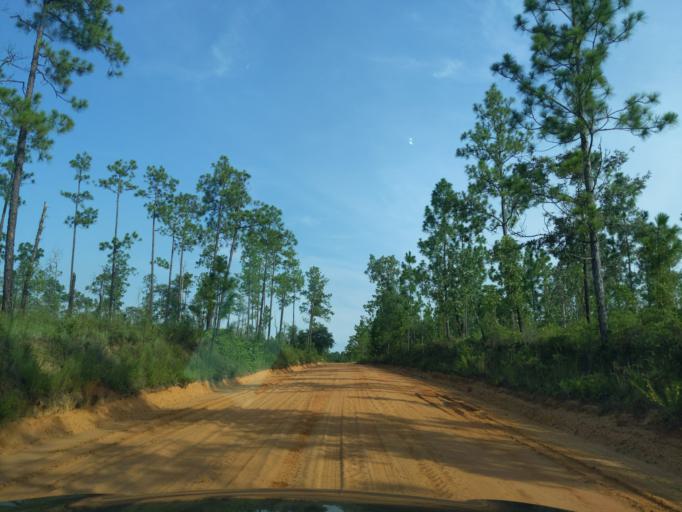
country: US
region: Florida
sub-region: Gadsden County
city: Midway
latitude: 30.4000
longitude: -84.4113
